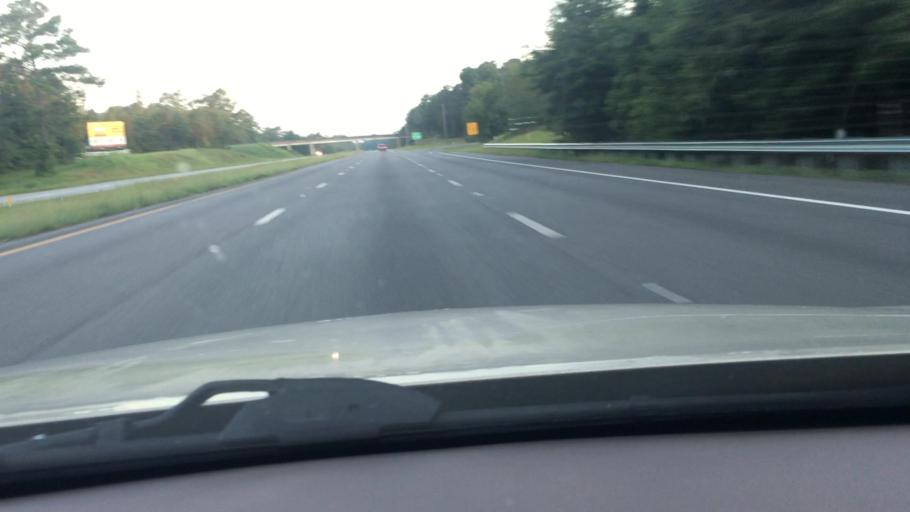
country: US
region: South Carolina
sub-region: Richland County
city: Lake Murray of Richland
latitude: 34.1444
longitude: -81.2344
